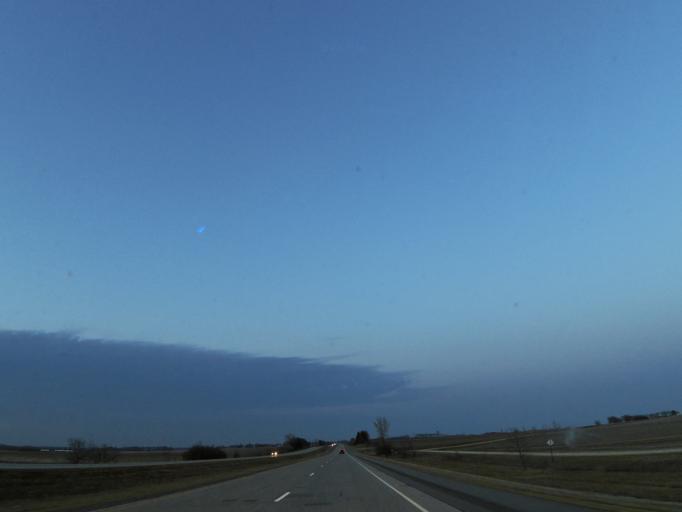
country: US
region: Minnesota
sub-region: Mower County
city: Grand Meadow
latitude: 43.7884
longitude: -92.6094
